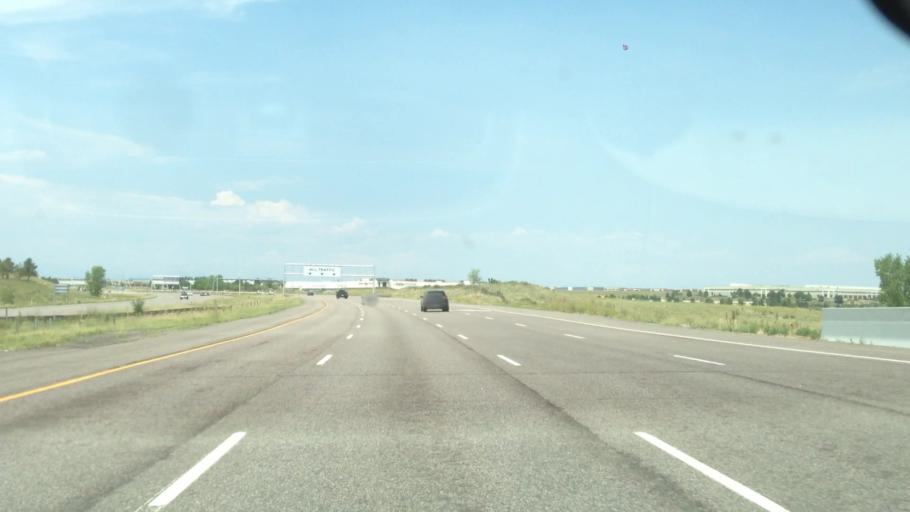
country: US
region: Colorado
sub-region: Douglas County
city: Stonegate
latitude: 39.5550
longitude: -104.8120
